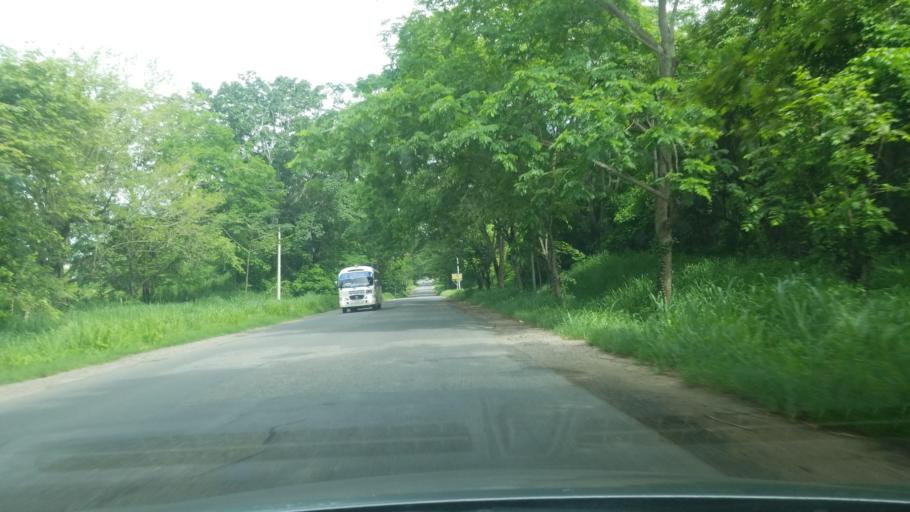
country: HN
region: Santa Barbara
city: Camalote
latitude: 15.3328
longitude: -88.3456
